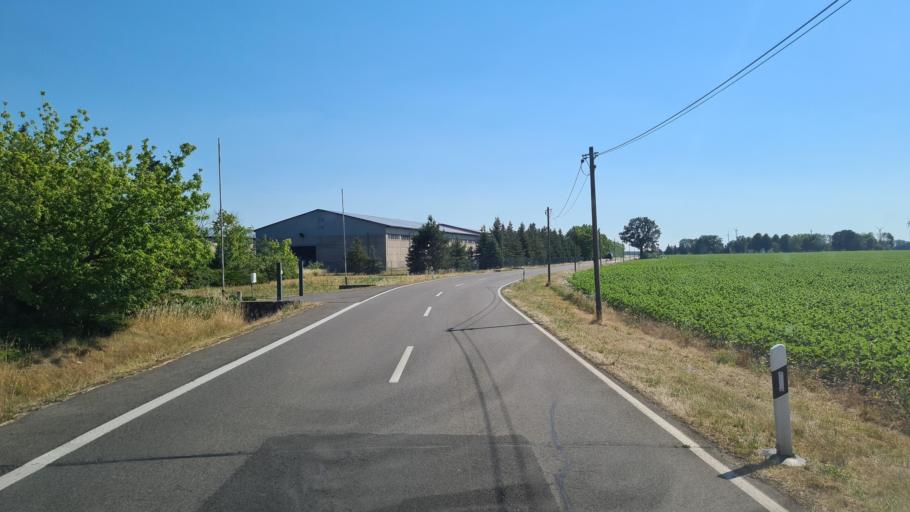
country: DE
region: Saxony-Anhalt
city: Annaburg
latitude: 51.6924
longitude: 12.9934
